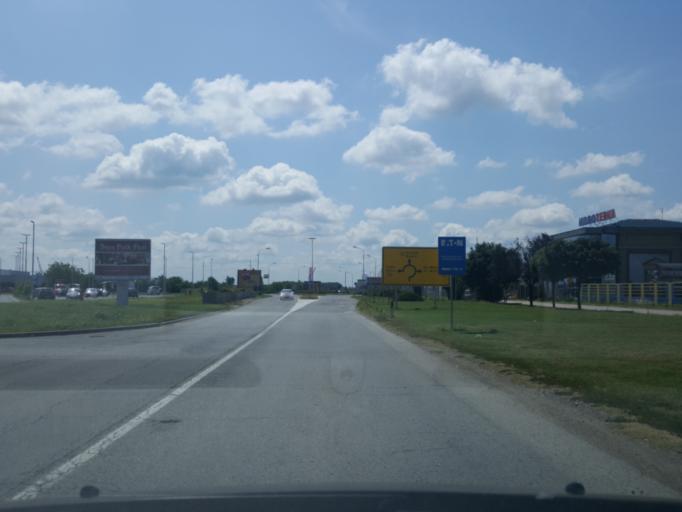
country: RS
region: Autonomna Pokrajina Vojvodina
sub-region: Sremski Okrug
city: Sremska Mitrovica
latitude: 44.9721
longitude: 19.6372
